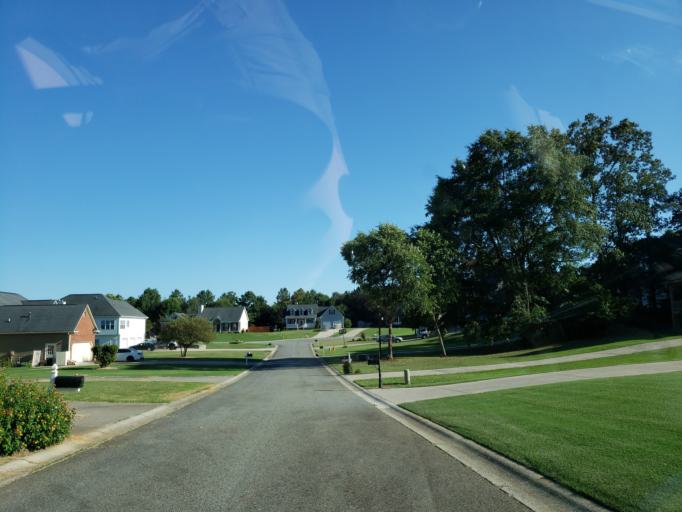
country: US
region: Georgia
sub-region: Bartow County
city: Euharlee
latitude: 34.1074
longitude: -84.9996
